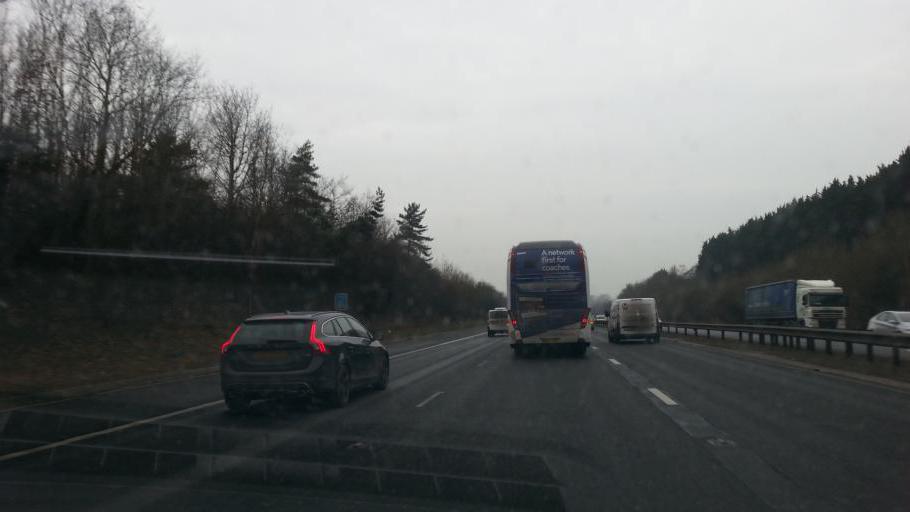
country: GB
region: England
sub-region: Hertfordshire
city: Sawbridgeworth
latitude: 51.8024
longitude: 0.1759
